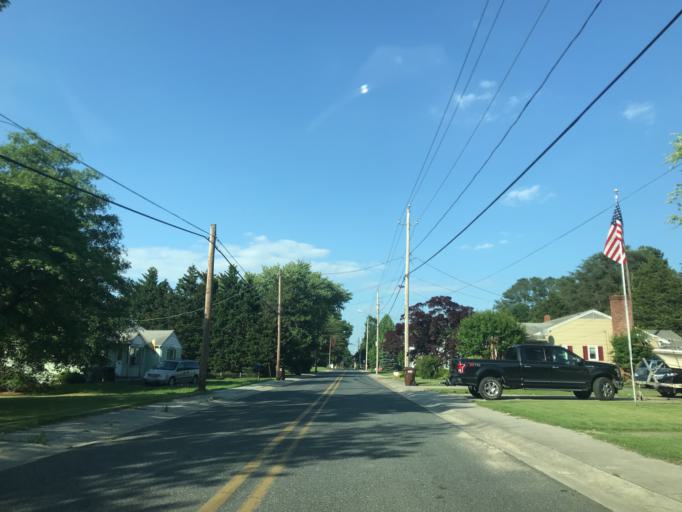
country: US
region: Maryland
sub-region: Wicomico County
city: Hebron
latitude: 38.5352
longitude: -75.7240
